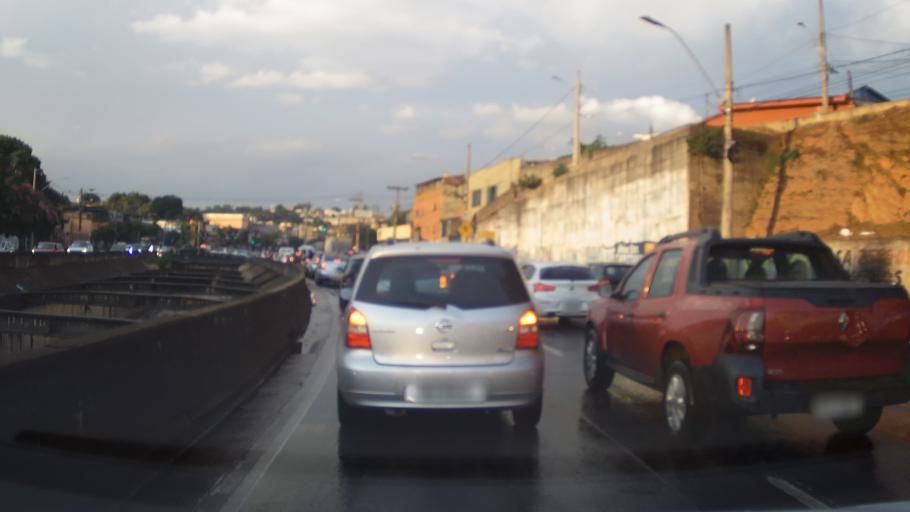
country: BR
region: Minas Gerais
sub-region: Belo Horizonte
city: Belo Horizonte
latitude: -19.9552
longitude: -43.9860
